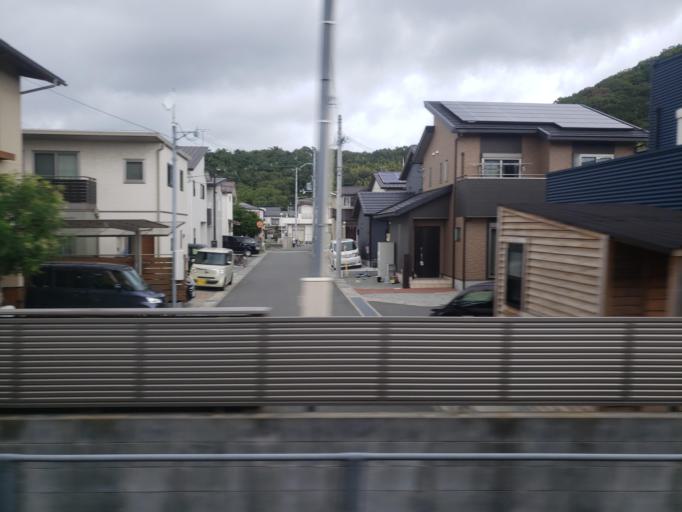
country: JP
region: Hyogo
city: Tatsunocho-tominaga
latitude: 34.8117
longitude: 134.6016
